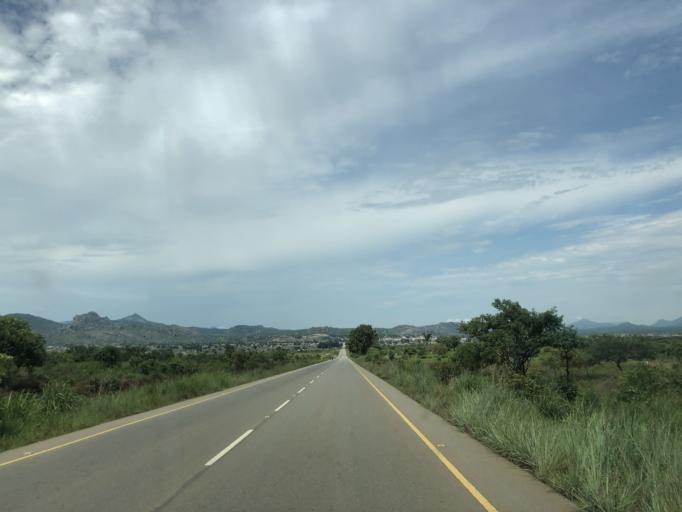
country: AO
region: Cuanza Sul
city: Quibala
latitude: -10.7339
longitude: 15.0119
